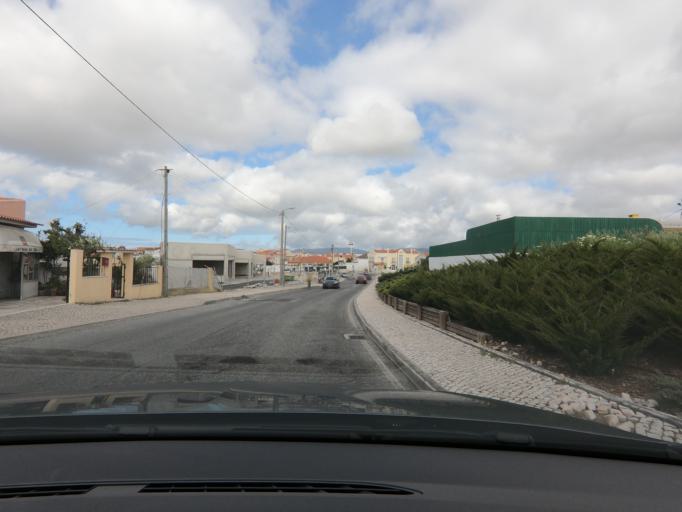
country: PT
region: Lisbon
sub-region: Cascais
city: Sao Domingos de Rana
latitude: 38.7145
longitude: -9.3430
